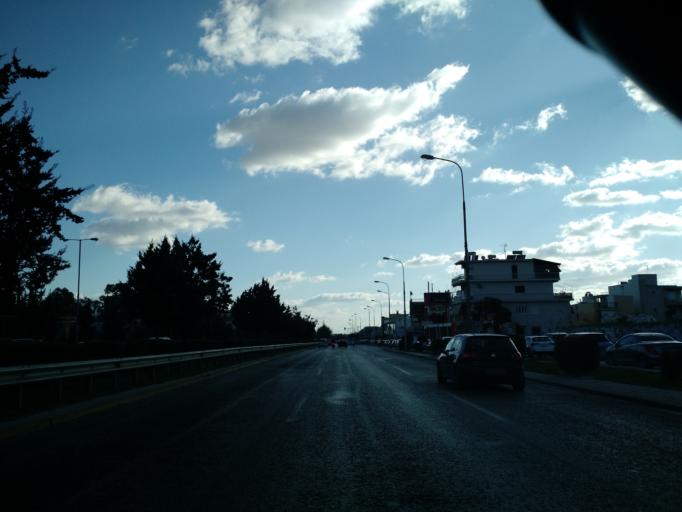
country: GR
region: Attica
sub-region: Nomarchia Athinas
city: Agios Dimitrios
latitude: 37.9224
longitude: 23.7442
